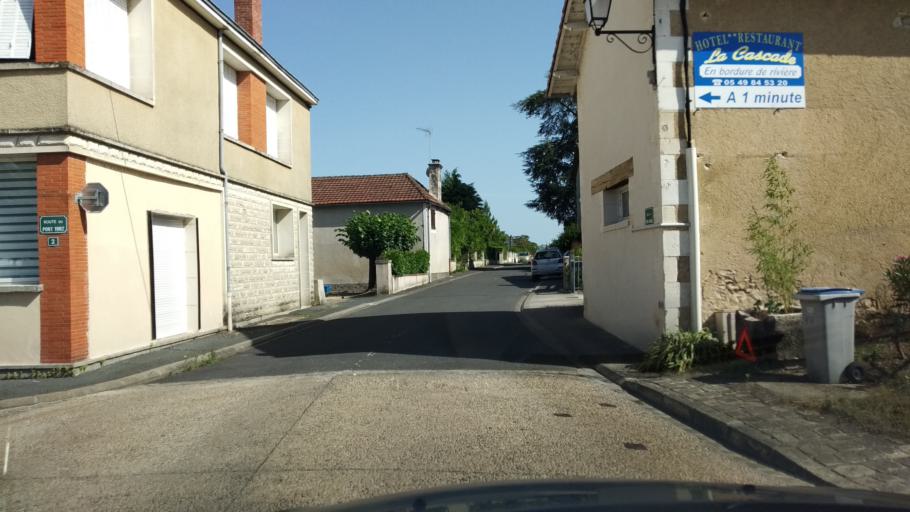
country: FR
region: Poitou-Charentes
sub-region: Departement de la Vienne
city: Lussac-les-Chateaux
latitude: 46.4440
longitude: 0.6665
